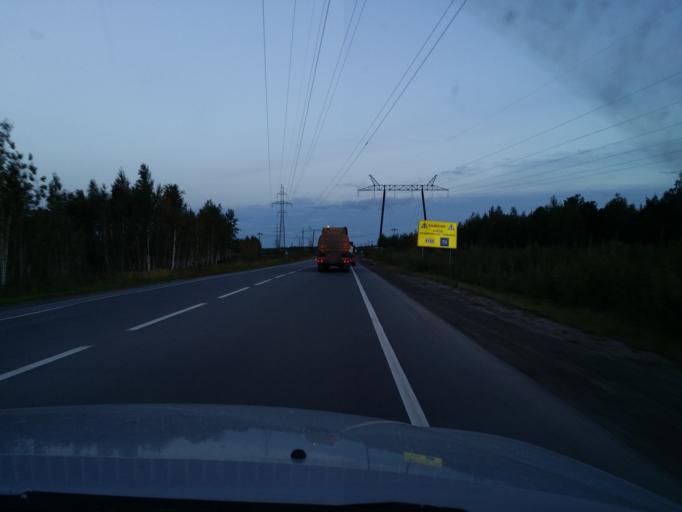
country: RU
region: Khanty-Mansiyskiy Avtonomnyy Okrug
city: Nizhnevartovsk
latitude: 61.0372
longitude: 76.3564
